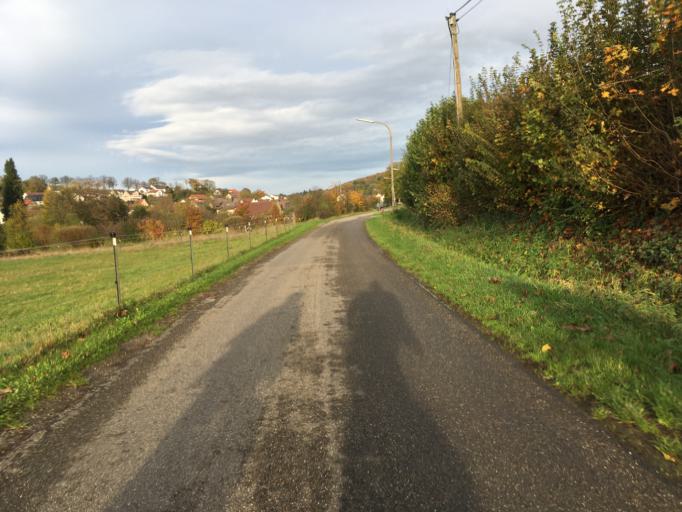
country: DE
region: Baden-Wuerttemberg
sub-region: Regierungsbezirk Stuttgart
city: Jagsthausen
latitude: 49.3623
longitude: 9.4819
